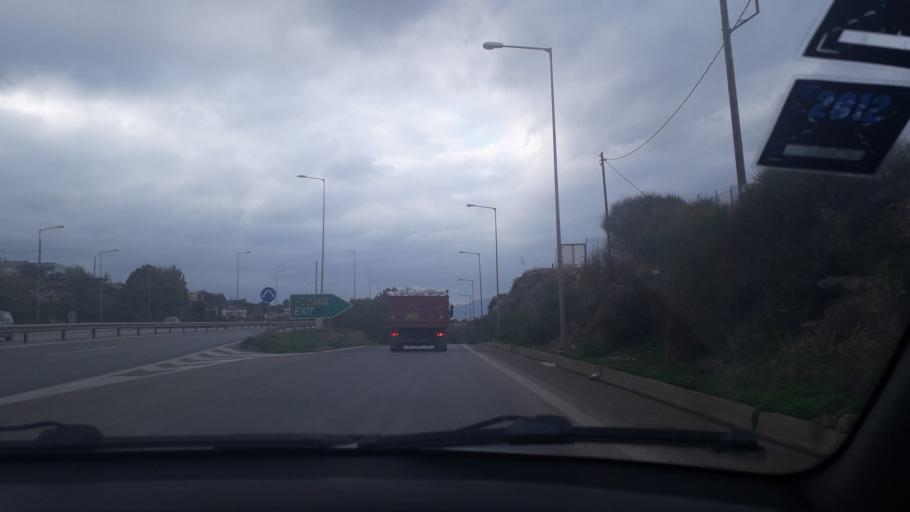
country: GR
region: Crete
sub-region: Nomos Rethymnis
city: Rethymno
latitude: 35.3562
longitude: 24.4694
